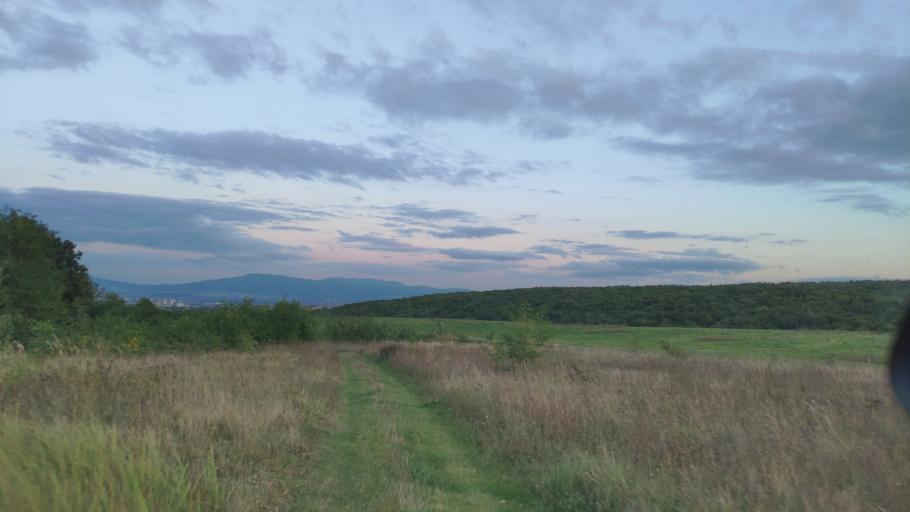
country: SK
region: Kosicky
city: Kosice
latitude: 48.7021
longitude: 21.2074
